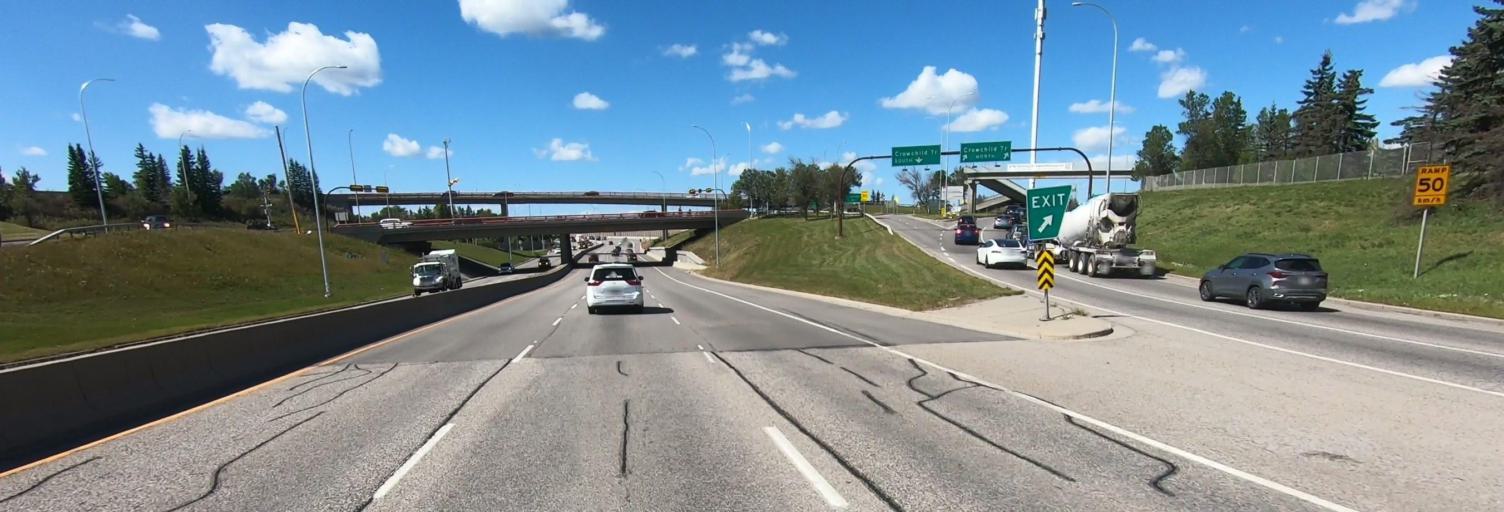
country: CA
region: Alberta
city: Calgary
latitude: 50.9993
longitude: -114.1151
